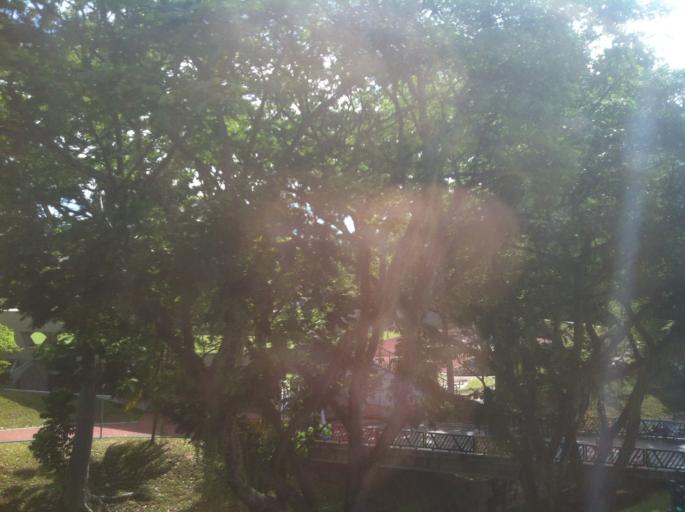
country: SG
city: Singapore
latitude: 1.3251
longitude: 103.9386
